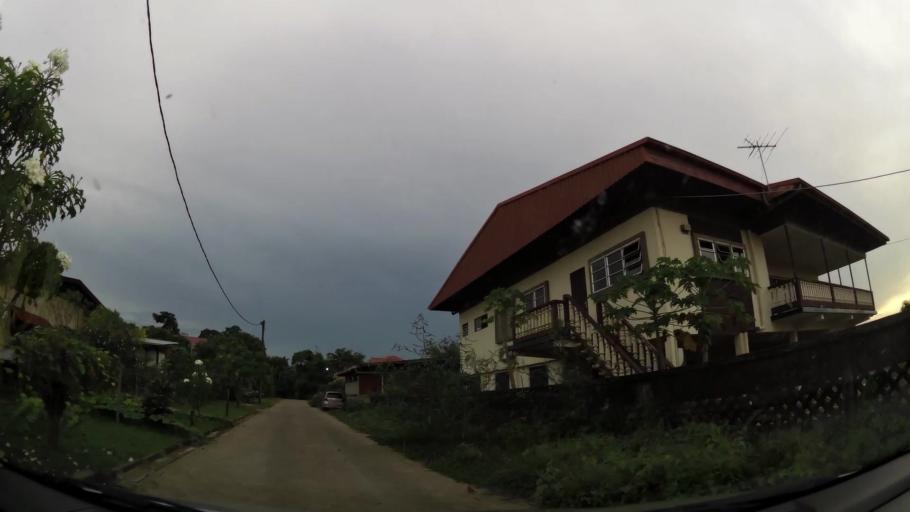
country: SR
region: Paramaribo
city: Paramaribo
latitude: 5.8275
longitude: -55.2005
